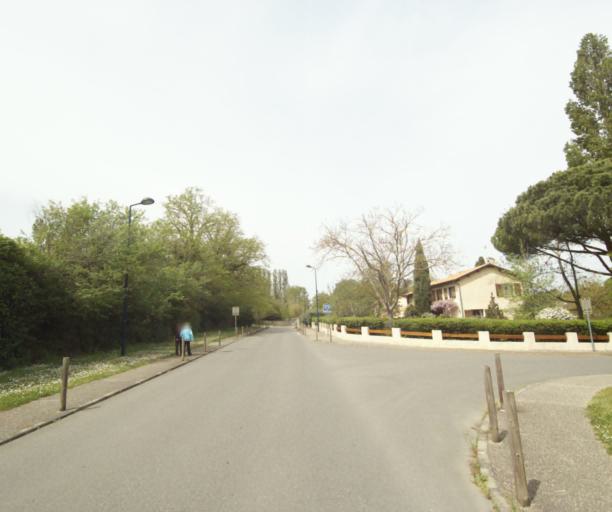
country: FR
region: Midi-Pyrenees
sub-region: Departement de la Haute-Garonne
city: Auzeville-Tolosane
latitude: 43.5242
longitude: 1.4880
